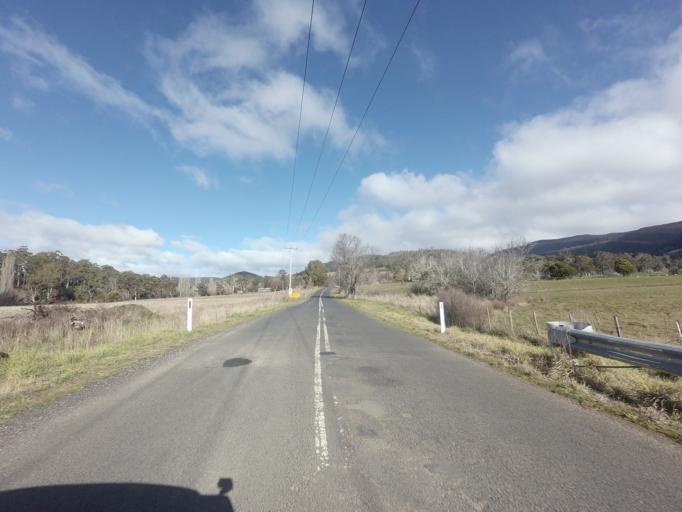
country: AU
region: Tasmania
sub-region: Derwent Valley
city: New Norfolk
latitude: -42.6001
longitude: 146.7068
